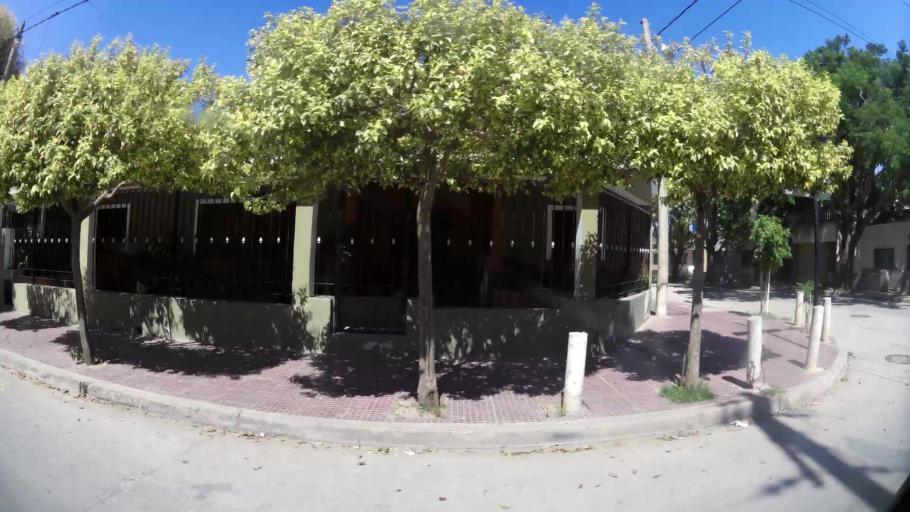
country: AR
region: Cordoba
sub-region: Departamento de Capital
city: Cordoba
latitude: -31.3735
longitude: -64.1365
